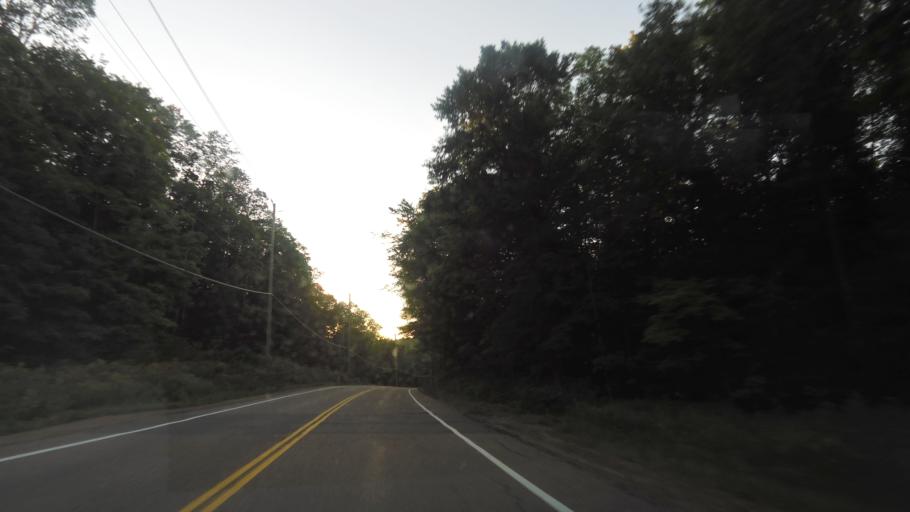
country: CA
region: Ontario
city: Bancroft
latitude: 45.0309
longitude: -78.4078
